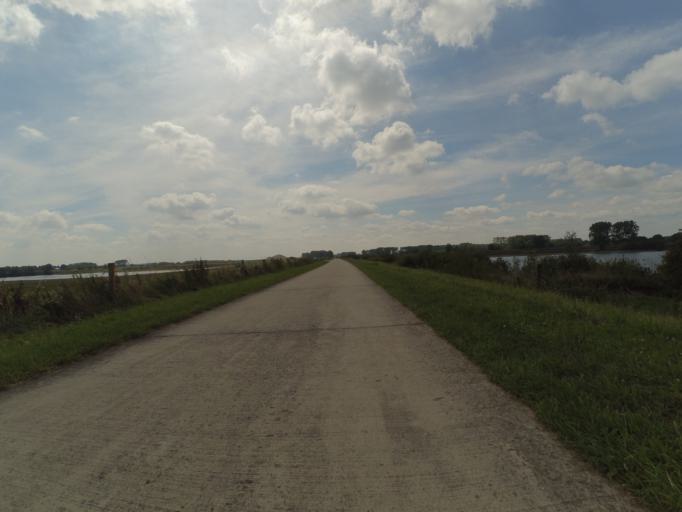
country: NL
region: Limburg
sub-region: Gemeente Stein
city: Berg
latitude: 51.0514
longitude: 5.7586
